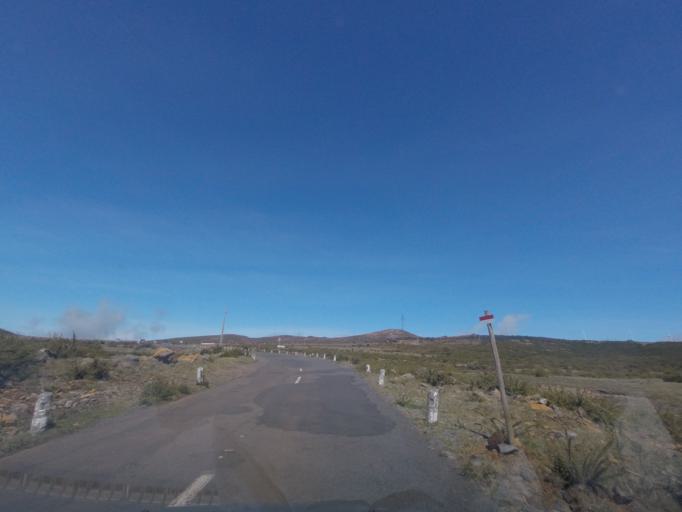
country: PT
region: Madeira
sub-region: Calheta
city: Arco da Calheta
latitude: 32.7563
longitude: -17.0972
